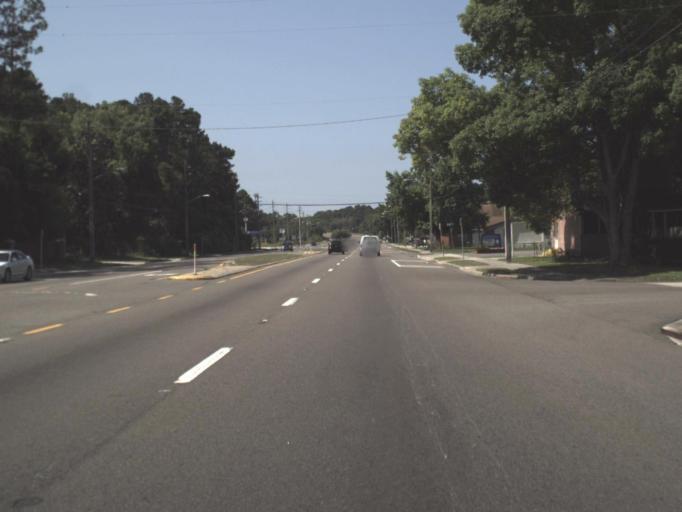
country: US
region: Florida
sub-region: Duval County
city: Jacksonville
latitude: 30.4243
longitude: -81.6956
